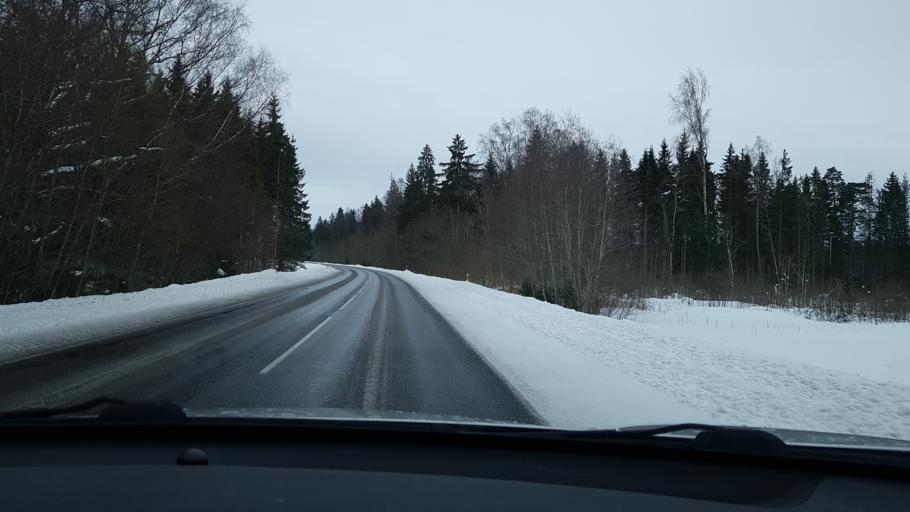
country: EE
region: Jaervamaa
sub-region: Jaerva-Jaani vald
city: Jarva-Jaani
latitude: 59.0986
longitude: 25.8185
